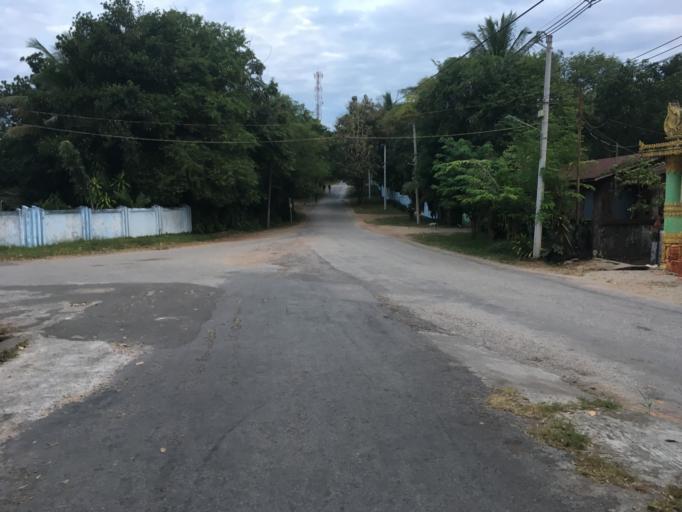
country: MM
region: Mon
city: Mawlamyine
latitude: 16.4758
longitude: 97.6298
